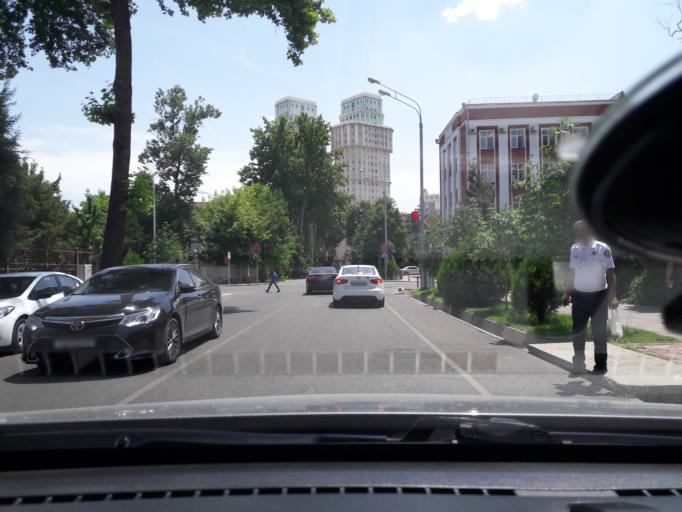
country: TJ
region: Dushanbe
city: Dushanbe
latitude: 38.5749
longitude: 68.7894
